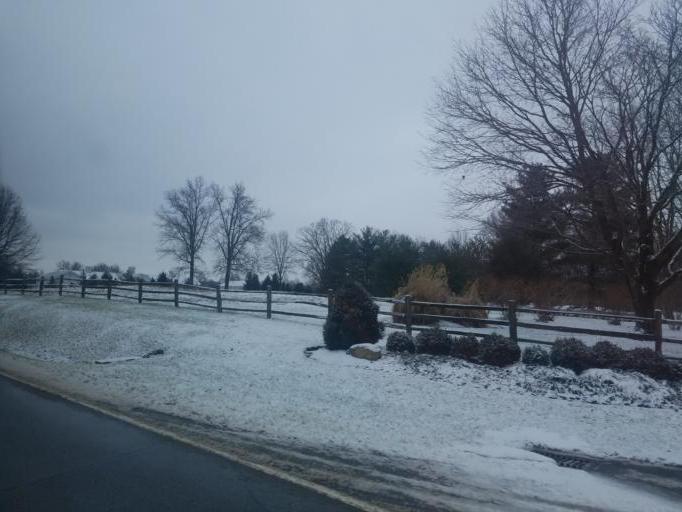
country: US
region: Ohio
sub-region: Franklin County
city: New Albany
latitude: 40.0655
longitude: -82.7957
